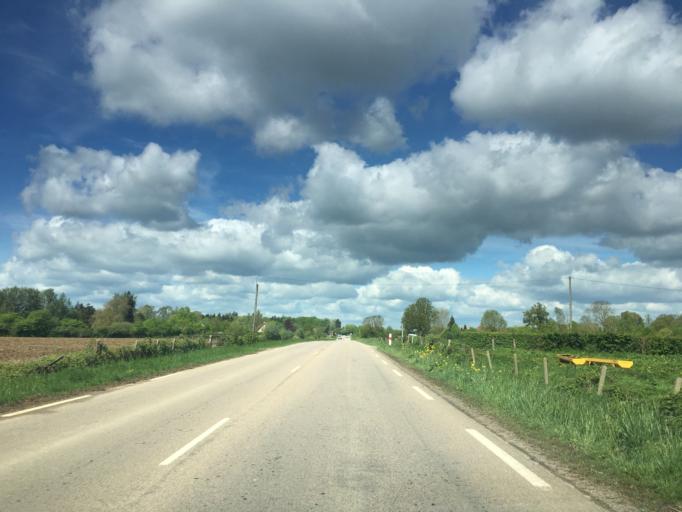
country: FR
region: Lower Normandy
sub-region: Departement de l'Orne
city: Aube-sur-Rile
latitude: 48.8379
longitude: 0.5250
